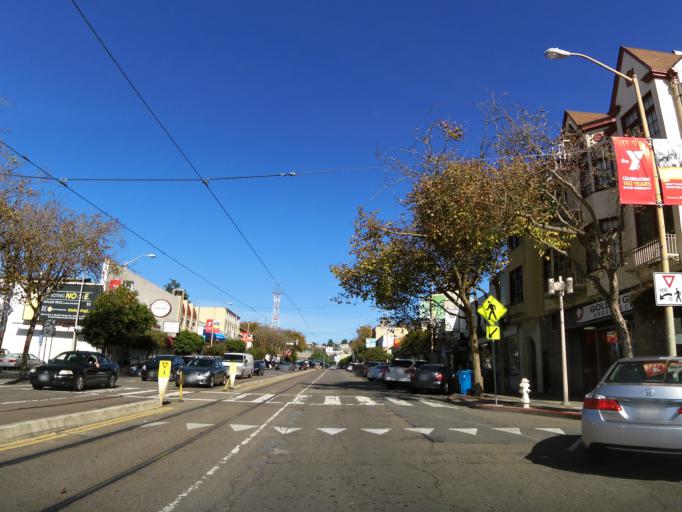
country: US
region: California
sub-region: San Mateo County
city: Daly City
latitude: 37.7388
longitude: -122.4681
